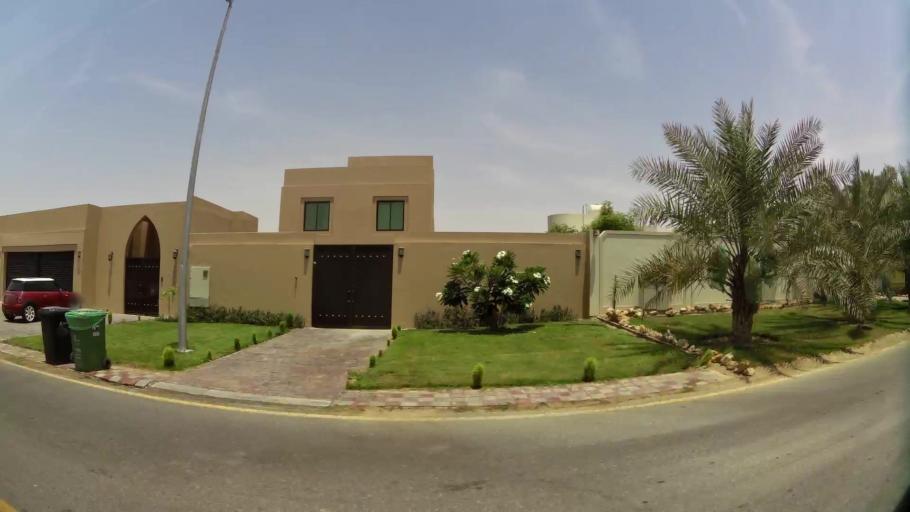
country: AE
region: Ash Shariqah
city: Sharjah
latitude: 25.2528
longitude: 55.4624
